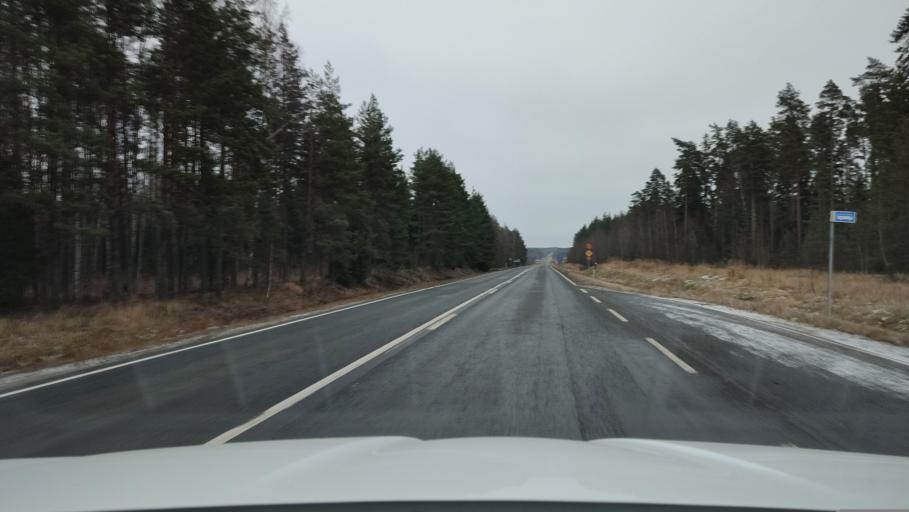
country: FI
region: Ostrobothnia
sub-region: Sydosterbotten
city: Naerpes
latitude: 62.3988
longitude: 21.3658
